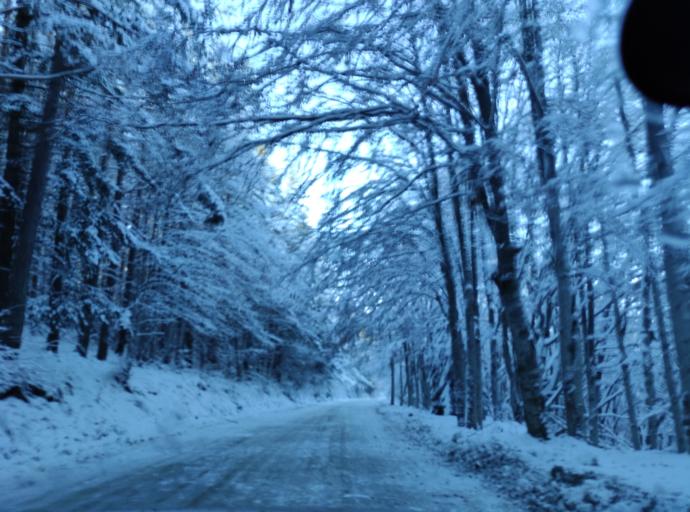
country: BG
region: Sofia-Capital
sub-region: Stolichna Obshtina
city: Sofia
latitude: 42.5958
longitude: 23.3087
